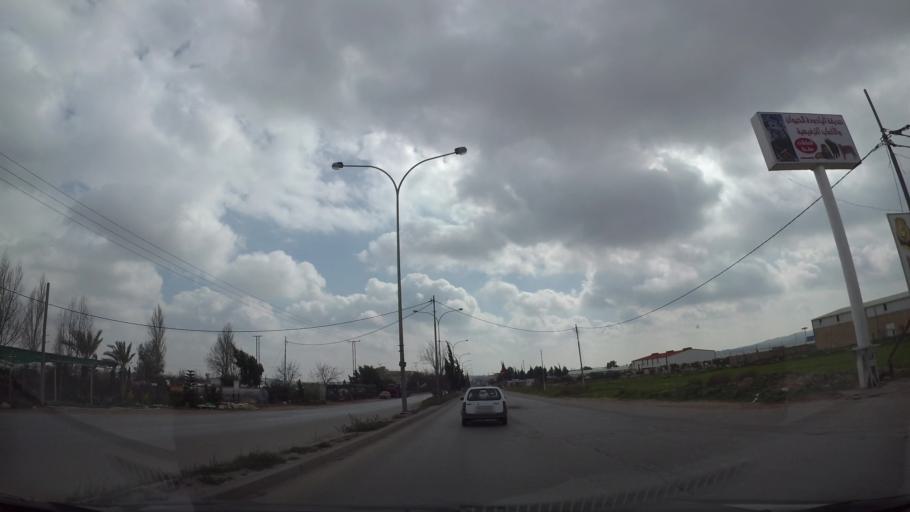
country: JO
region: Amman
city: Jawa
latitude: 31.8309
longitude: 35.9127
